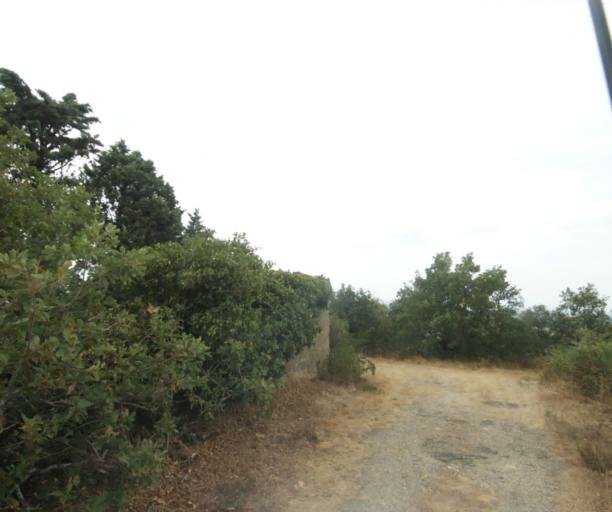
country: FR
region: Midi-Pyrenees
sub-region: Departement de la Haute-Garonne
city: Revel
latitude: 43.4449
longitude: 2.0098
